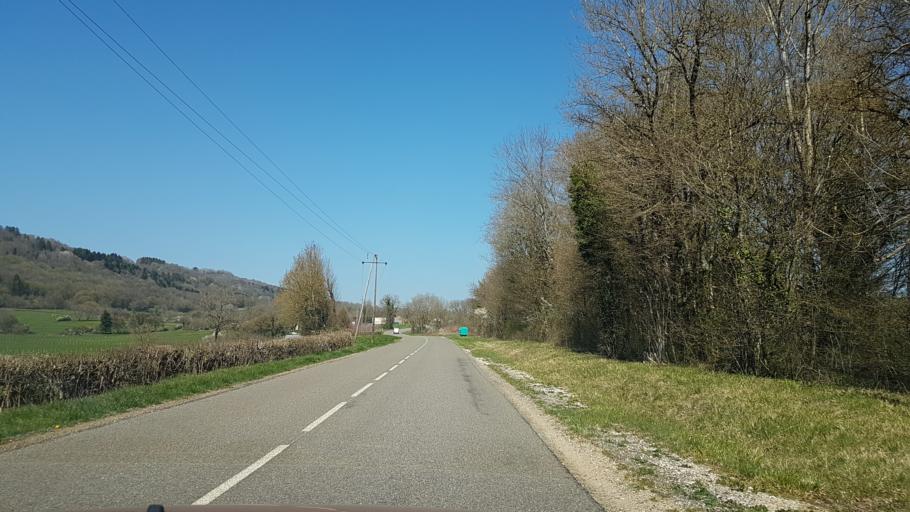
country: FR
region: Bourgogne
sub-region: Departement de Saone-et-Loire
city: Cuiseaux
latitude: 46.4727
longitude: 5.4526
